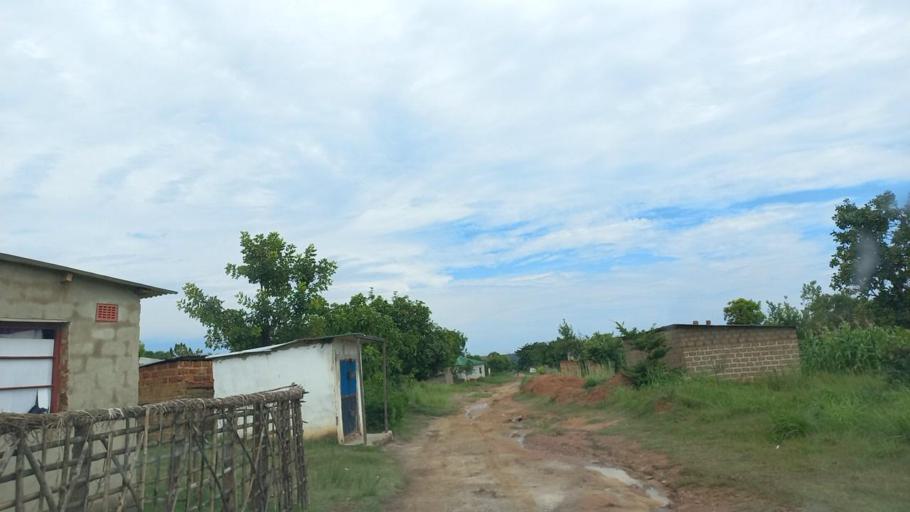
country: ZM
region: Copperbelt
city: Kitwe
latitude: -12.8664
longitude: 28.3350
